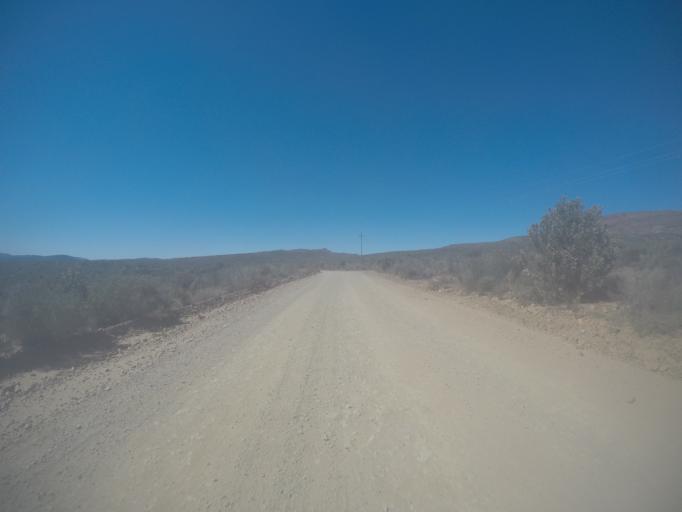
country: ZA
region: Western Cape
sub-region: West Coast District Municipality
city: Clanwilliam
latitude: -32.4993
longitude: 19.2759
